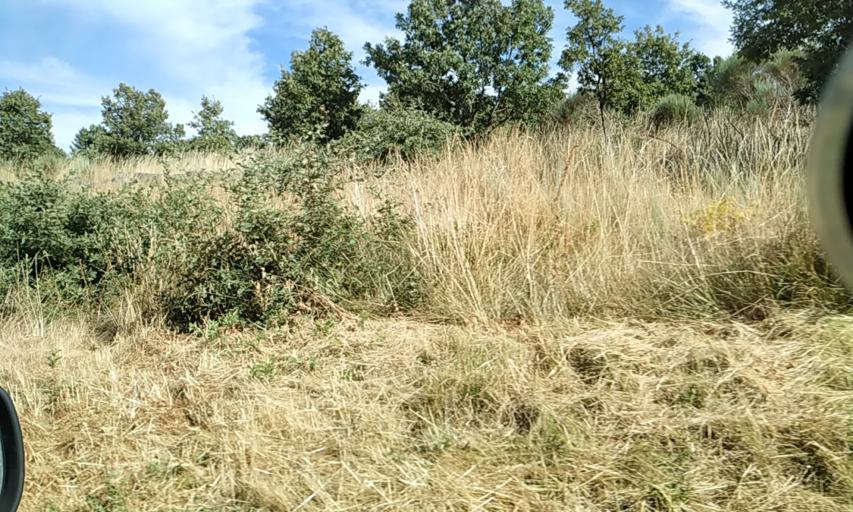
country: PT
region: Vila Real
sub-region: Murca
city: Murca
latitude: 41.3762
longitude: -7.5542
